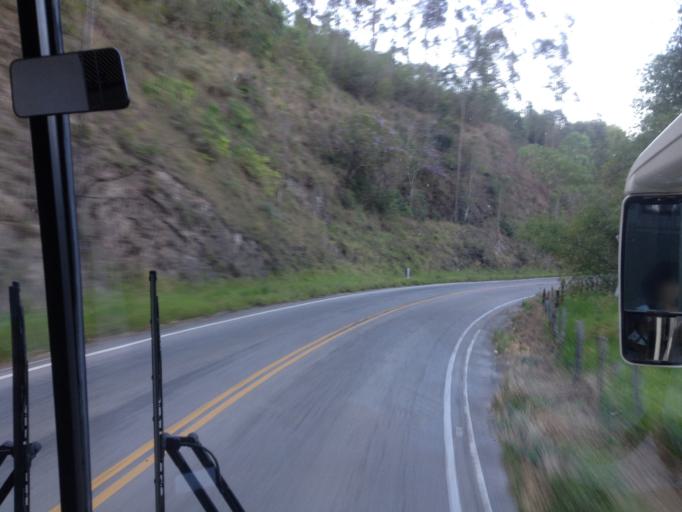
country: BR
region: Minas Gerais
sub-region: Juiz De Fora
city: Juiz de Fora
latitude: -21.6536
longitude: -43.3339
